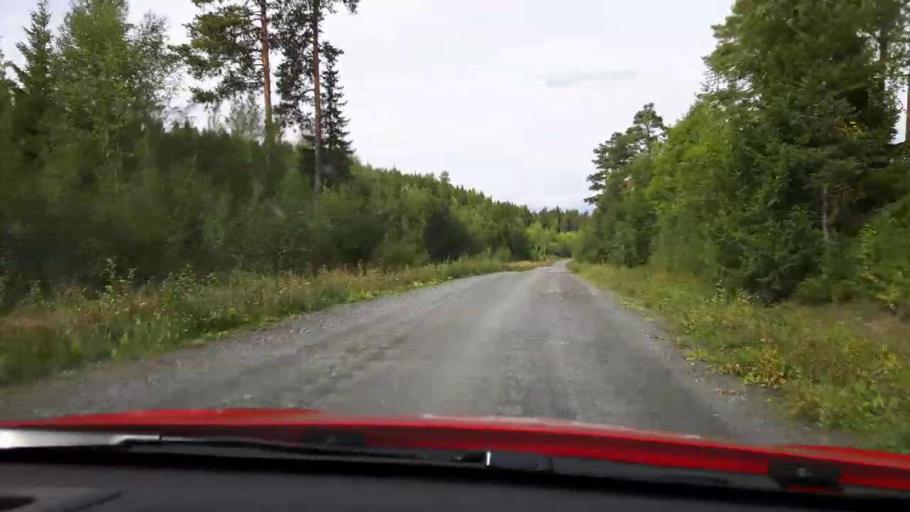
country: SE
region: Jaemtland
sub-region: Are Kommun
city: Jarpen
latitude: 63.2745
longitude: 13.7413
